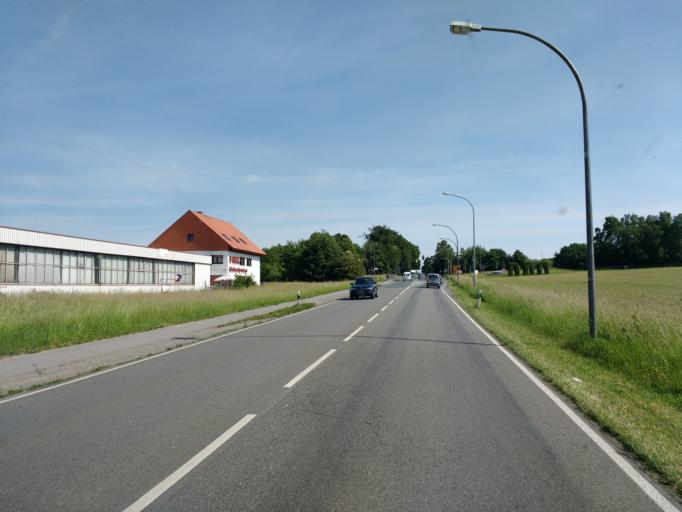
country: DE
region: North Rhine-Westphalia
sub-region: Regierungsbezirk Detmold
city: Bad Salzuflen
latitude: 52.0693
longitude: 8.7376
